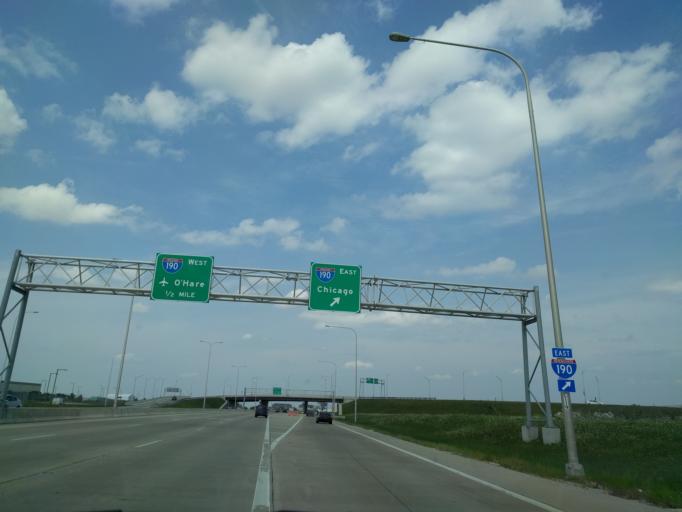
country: US
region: Illinois
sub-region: Cook County
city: Schiller Park
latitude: 41.9747
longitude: -87.8781
